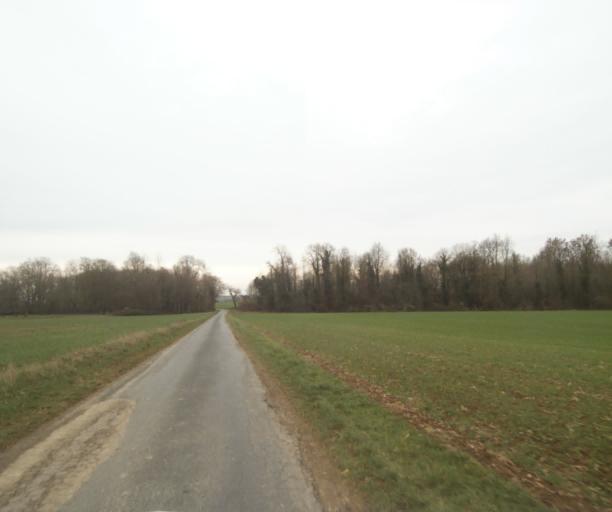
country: FR
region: Champagne-Ardenne
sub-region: Departement de la Haute-Marne
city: Villiers-en-Lieu
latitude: 48.6354
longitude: 4.8082
